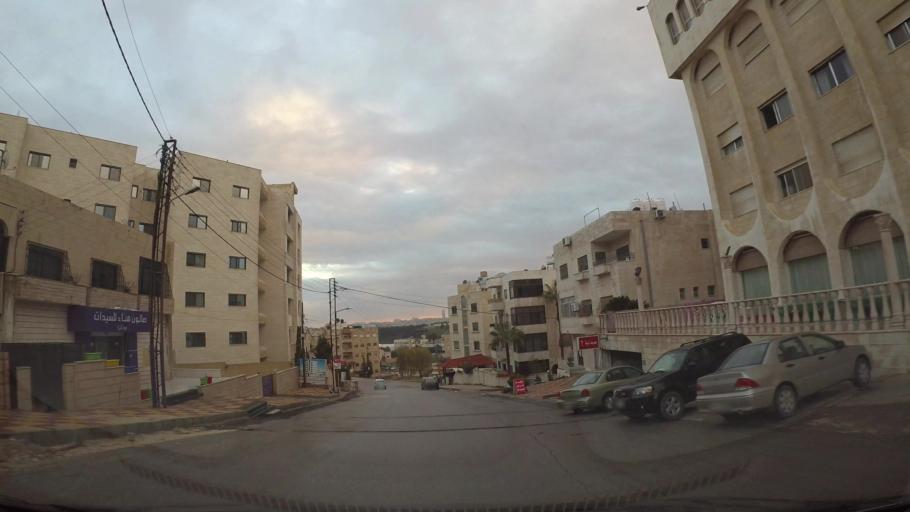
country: JO
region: Amman
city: Amman
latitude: 31.9894
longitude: 35.9126
